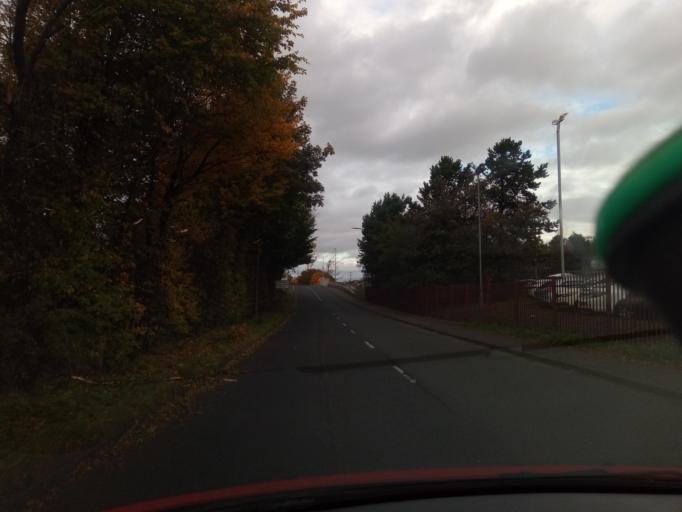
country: GB
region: Scotland
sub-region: West Lothian
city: Blackburn
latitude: 55.8403
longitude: -3.6137
